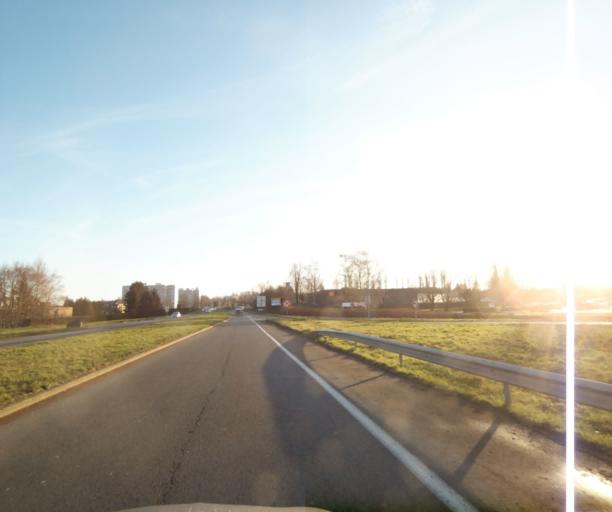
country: FR
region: Nord-Pas-de-Calais
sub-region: Departement du Nord
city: Famars
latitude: 50.3355
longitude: 3.5129
